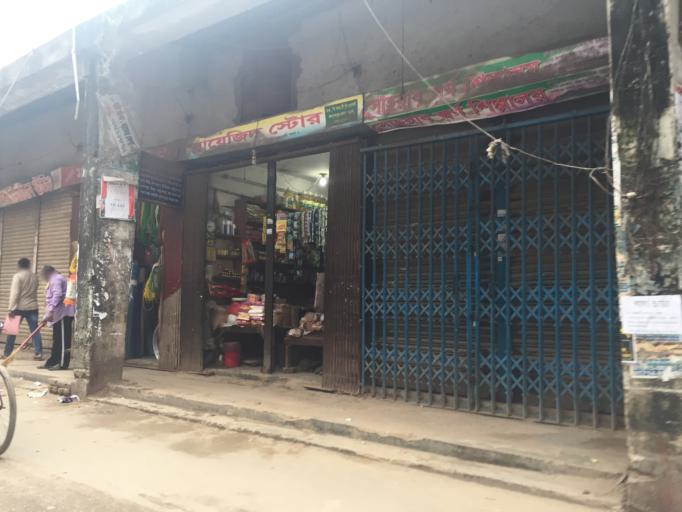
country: BD
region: Dhaka
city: Azimpur
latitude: 23.7798
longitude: 90.3611
